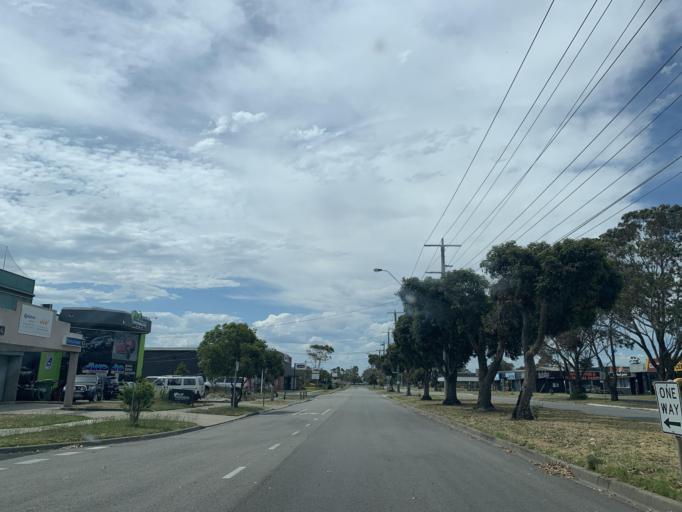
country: AU
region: Victoria
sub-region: Frankston
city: Frankston North
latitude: -38.1143
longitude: 145.1412
